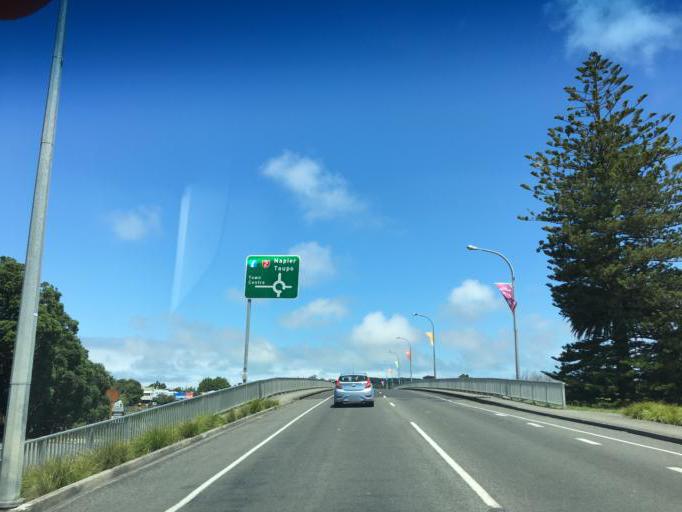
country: NZ
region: Hawke's Bay
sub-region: Wairoa District
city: Wairoa
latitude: -39.0304
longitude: 177.4190
